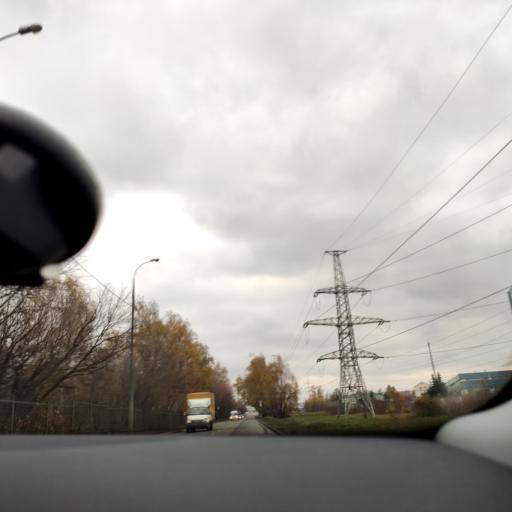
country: RU
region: Moscow
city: Kapotnya
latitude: 55.6659
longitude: 37.8081
